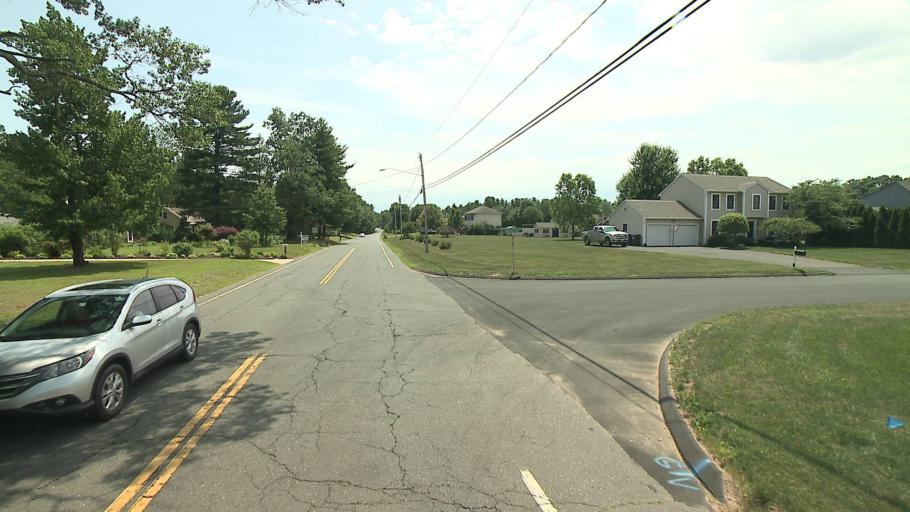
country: US
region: Massachusetts
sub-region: Hampden County
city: Southwick
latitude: 42.0268
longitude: -72.7489
